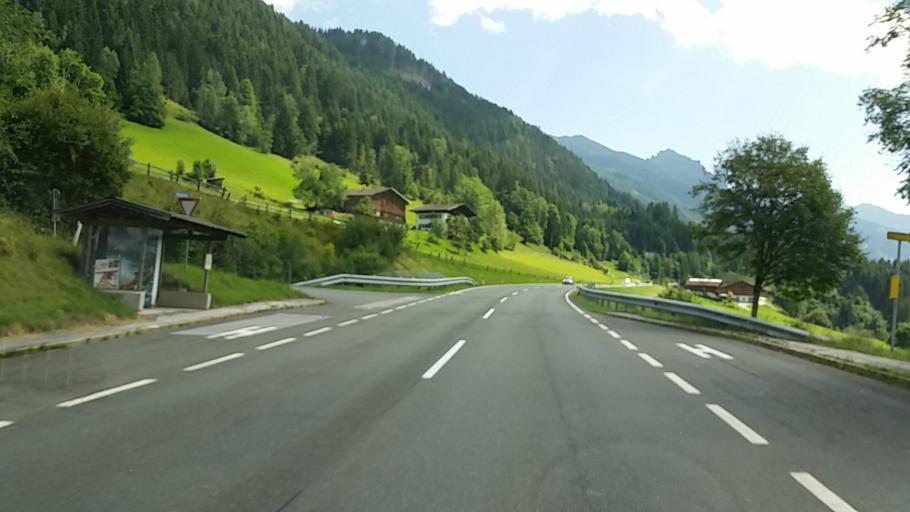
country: AT
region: Salzburg
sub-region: Politischer Bezirk Sankt Johann im Pongau
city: Forstau
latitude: 47.3538
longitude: 13.4984
